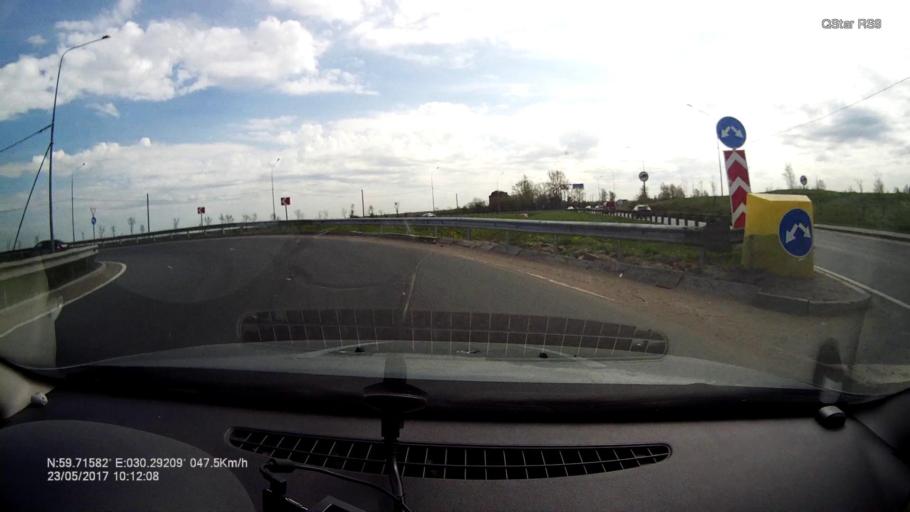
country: RU
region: St.-Petersburg
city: Aleksandrovskaya
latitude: 59.7159
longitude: 30.2920
